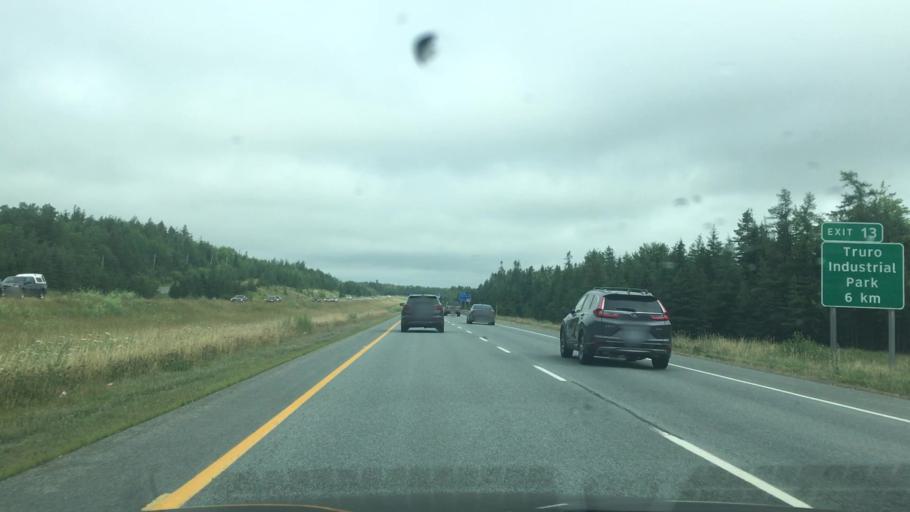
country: CA
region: Nova Scotia
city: Truro
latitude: 45.2926
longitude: -63.3006
